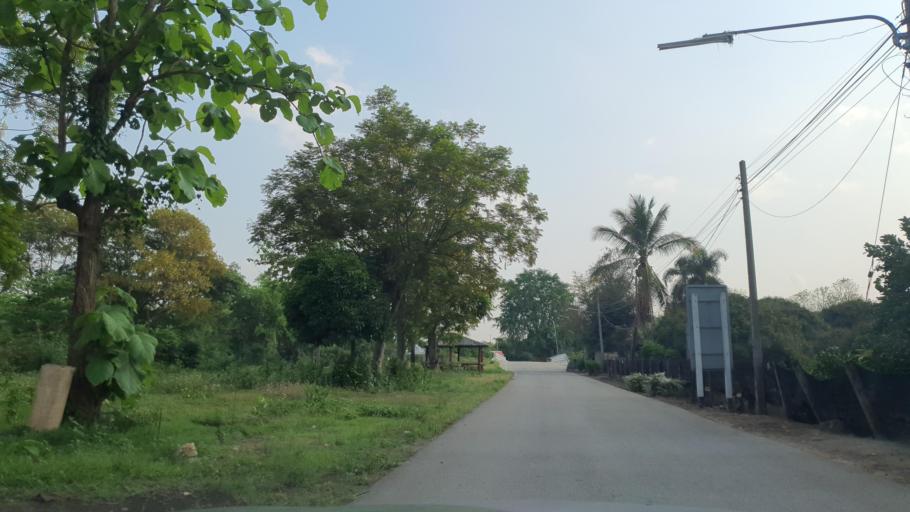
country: TH
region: Chiang Mai
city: Mae Wang
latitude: 18.6928
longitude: 98.8091
